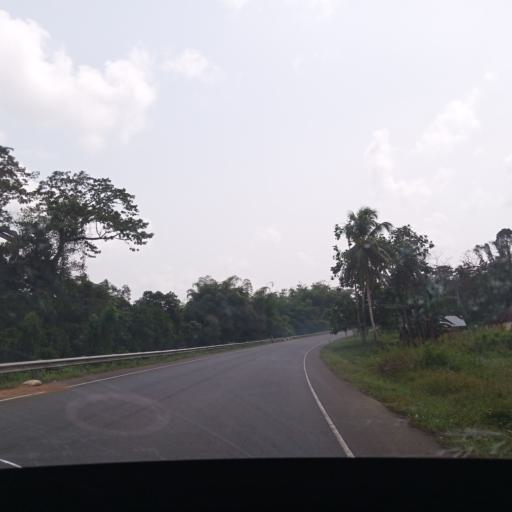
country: LR
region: Margibi
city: Kakata
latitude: 6.2418
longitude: -10.2865
